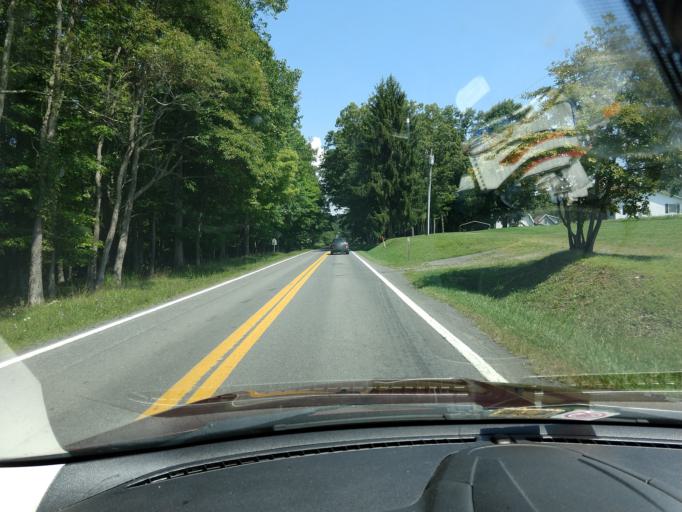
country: US
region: West Virginia
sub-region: Greenbrier County
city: Fairlea
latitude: 37.8253
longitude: -80.5593
